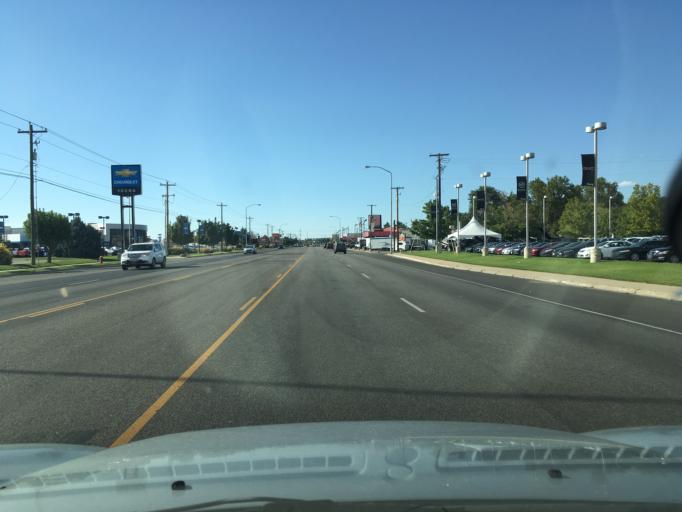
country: US
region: Utah
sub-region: Davis County
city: Layton
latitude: 41.0680
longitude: -111.9738
